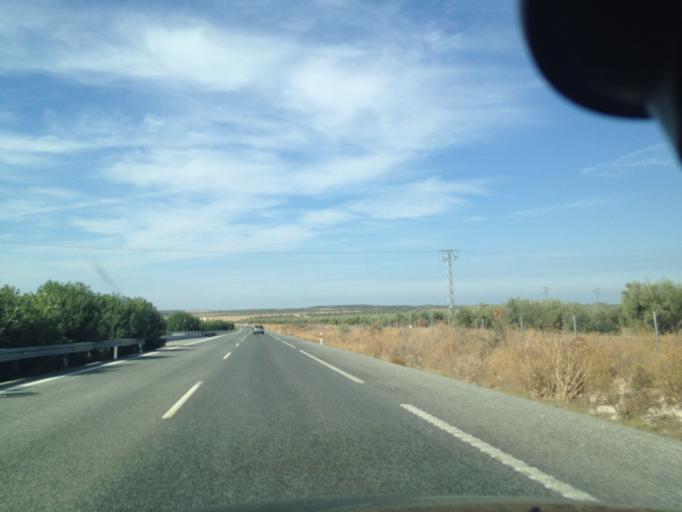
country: ES
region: Andalusia
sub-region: Provincia de Sevilla
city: La Puebla de Cazalla
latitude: 37.2321
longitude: -5.2220
